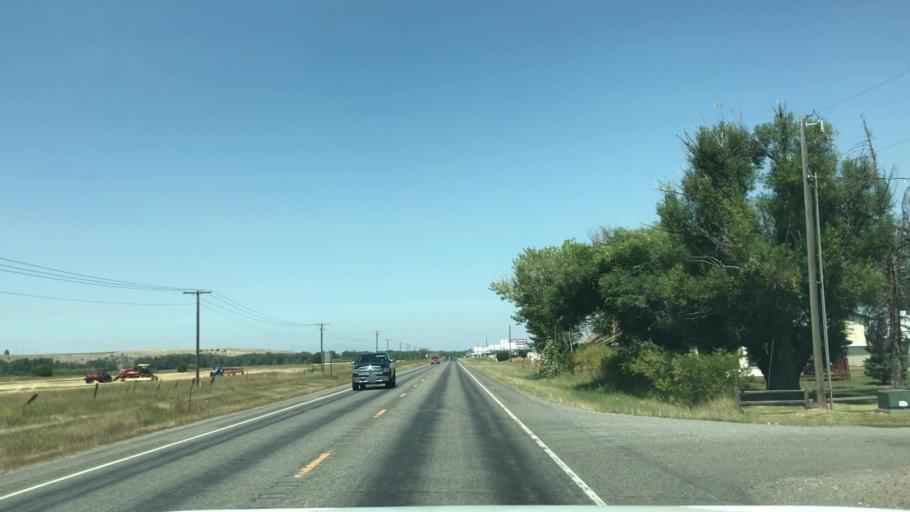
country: US
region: Montana
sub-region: Gallatin County
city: Four Corners
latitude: 45.6273
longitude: -111.1969
